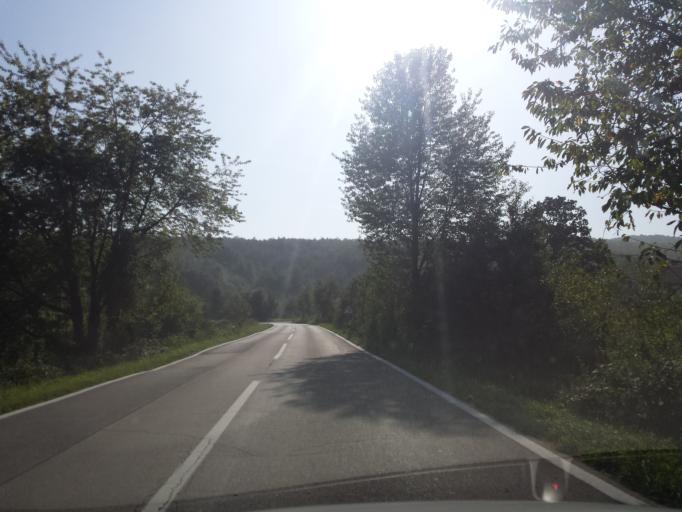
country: HR
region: Karlovacka
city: Ostarije
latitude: 45.2437
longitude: 15.3338
